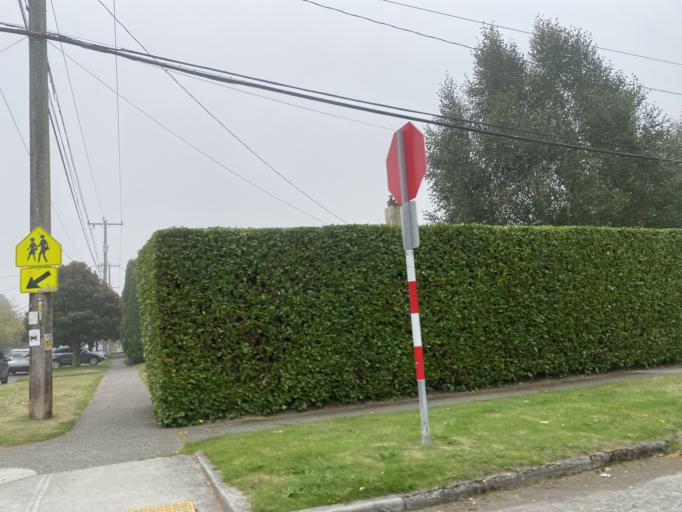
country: US
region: Washington
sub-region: King County
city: Seattle
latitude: 47.6486
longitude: -122.3983
